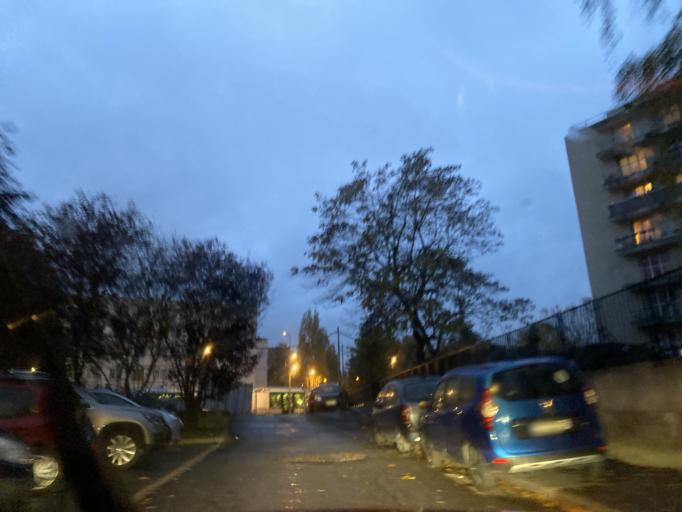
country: FR
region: Ile-de-France
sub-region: Departement des Hauts-de-Seine
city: Meudon
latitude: 48.7851
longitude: 2.2350
